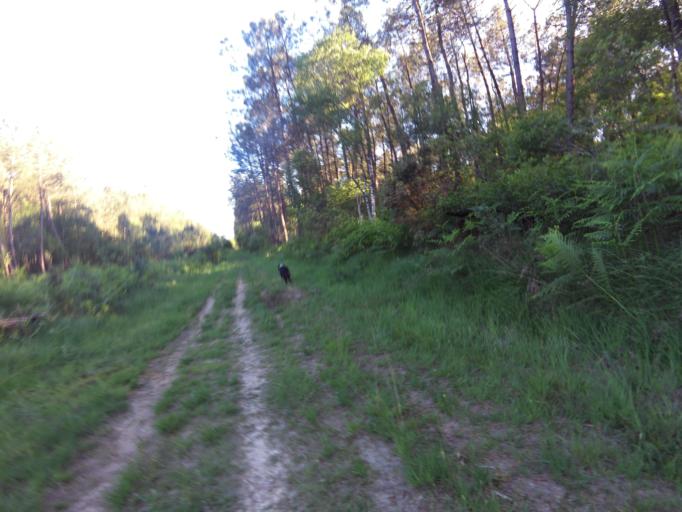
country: FR
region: Brittany
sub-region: Departement du Morbihan
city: Molac
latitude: 47.7451
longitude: -2.4301
